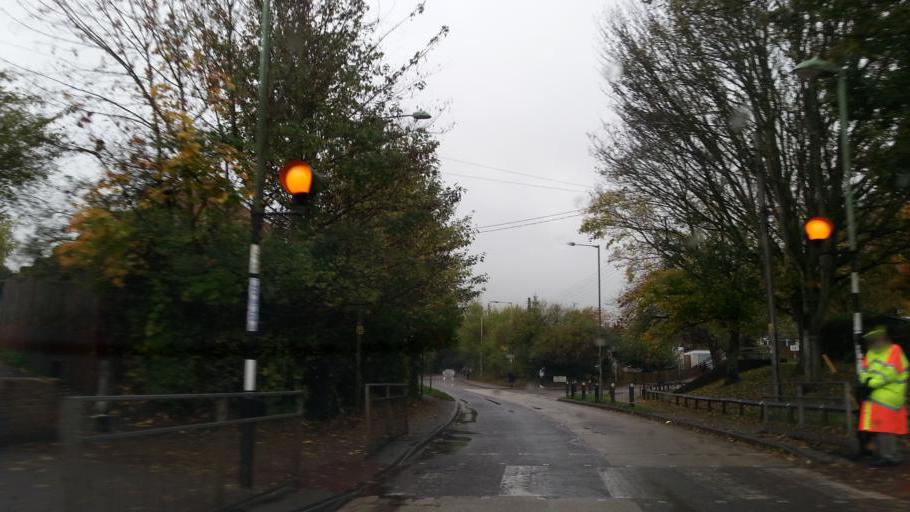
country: GB
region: England
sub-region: Suffolk
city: Haverhill
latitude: 52.0811
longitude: 0.4237
